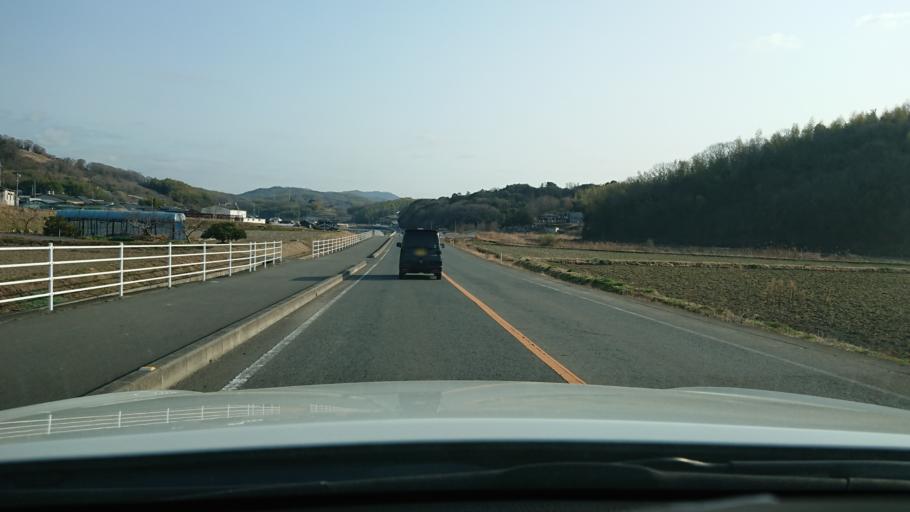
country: JP
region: Okayama
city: Kurashiki
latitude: 34.6025
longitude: 133.7026
